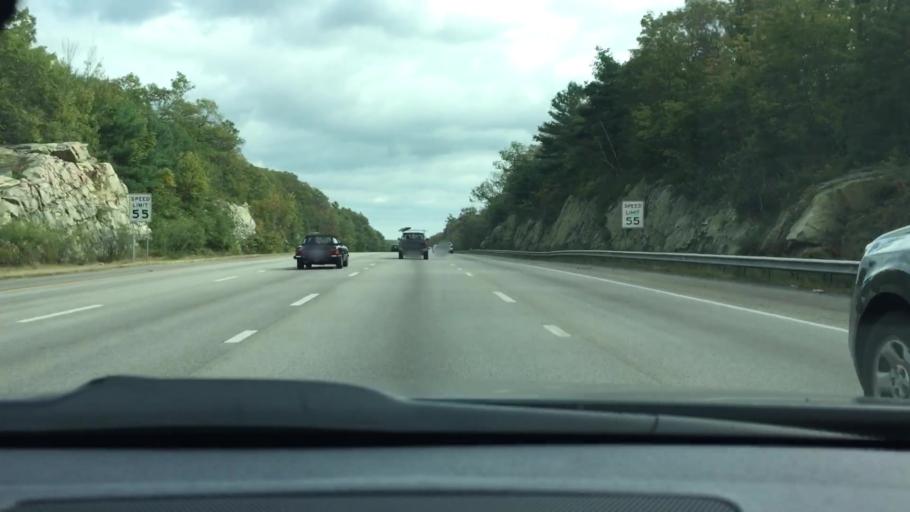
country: US
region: Massachusetts
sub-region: Norfolk County
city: Dedham
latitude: 42.2379
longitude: -71.1996
